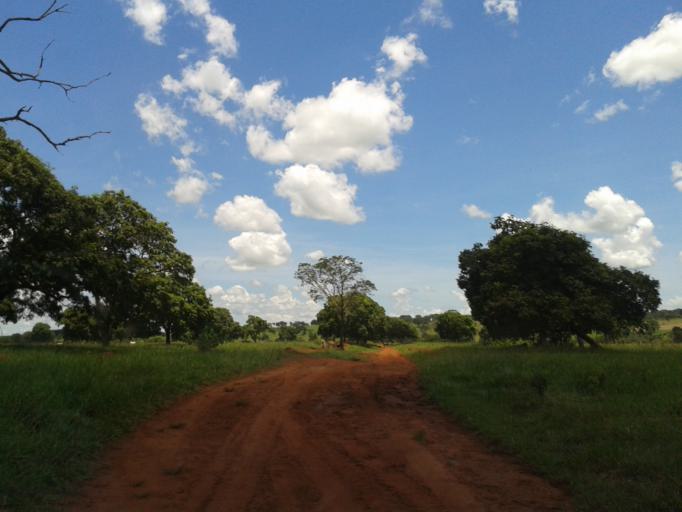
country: BR
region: Minas Gerais
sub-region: Santa Vitoria
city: Santa Vitoria
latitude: -18.7924
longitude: -49.8592
